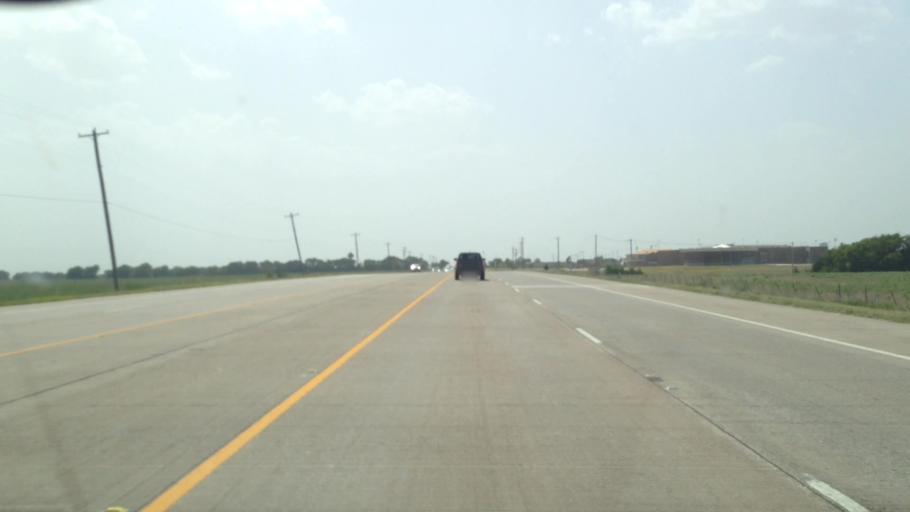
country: US
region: Texas
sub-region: Collin County
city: Princeton
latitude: 33.1715
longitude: -96.4791
